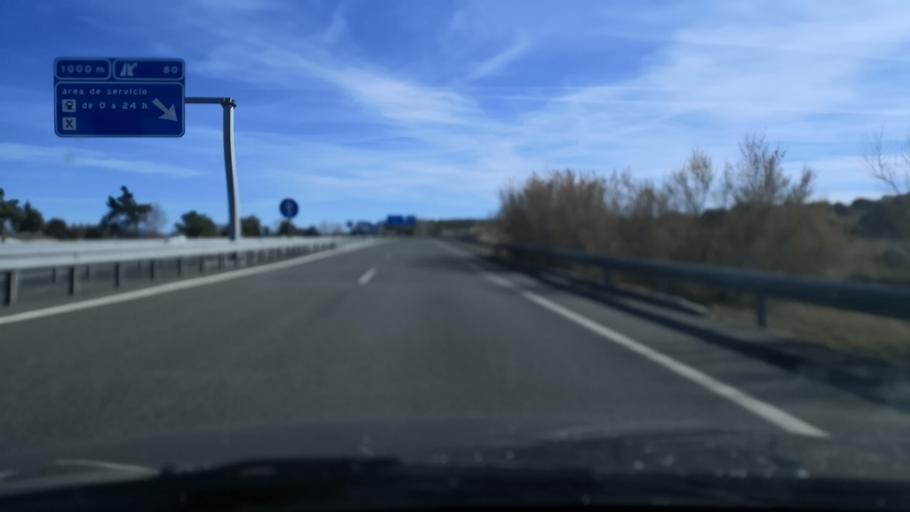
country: ES
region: Castille and Leon
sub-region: Provincia de Segovia
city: Villacastin
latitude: 40.7727
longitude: -4.4147
